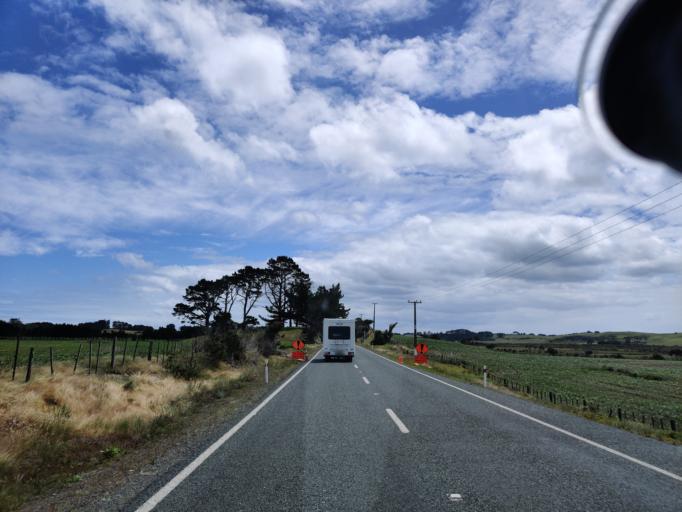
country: NZ
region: Northland
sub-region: Far North District
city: Kaitaia
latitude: -34.7795
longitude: 173.0945
